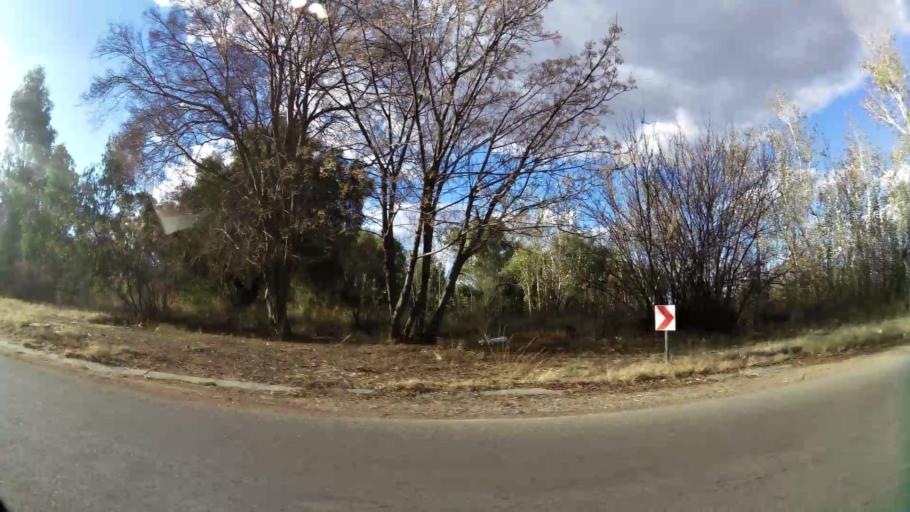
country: ZA
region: North-West
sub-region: Dr Kenneth Kaunda District Municipality
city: Potchefstroom
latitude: -26.7103
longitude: 27.0815
